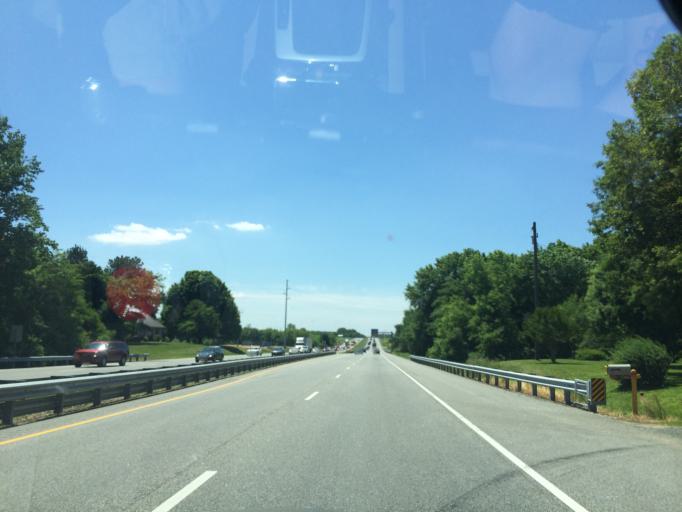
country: US
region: Maryland
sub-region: Talbot County
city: Easton
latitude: 38.8414
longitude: -76.0607
